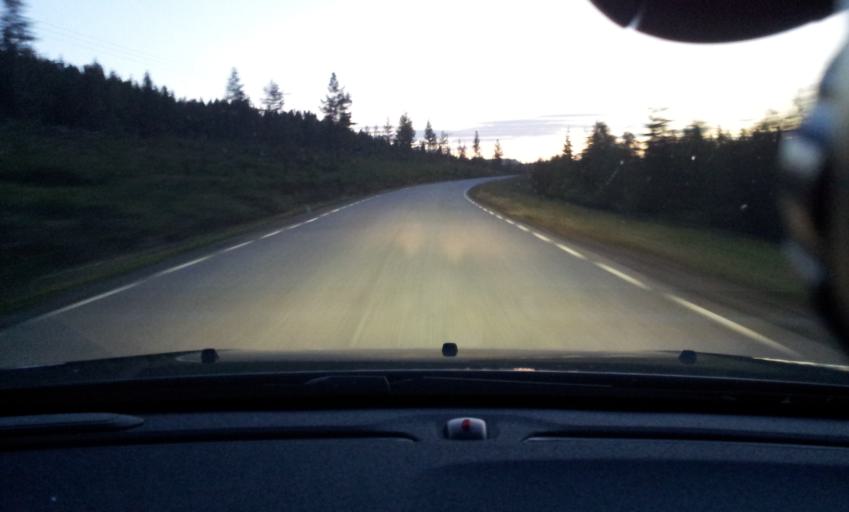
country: SE
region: Jaemtland
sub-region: Bergs Kommun
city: Hoverberg
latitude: 62.7082
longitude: 14.6141
